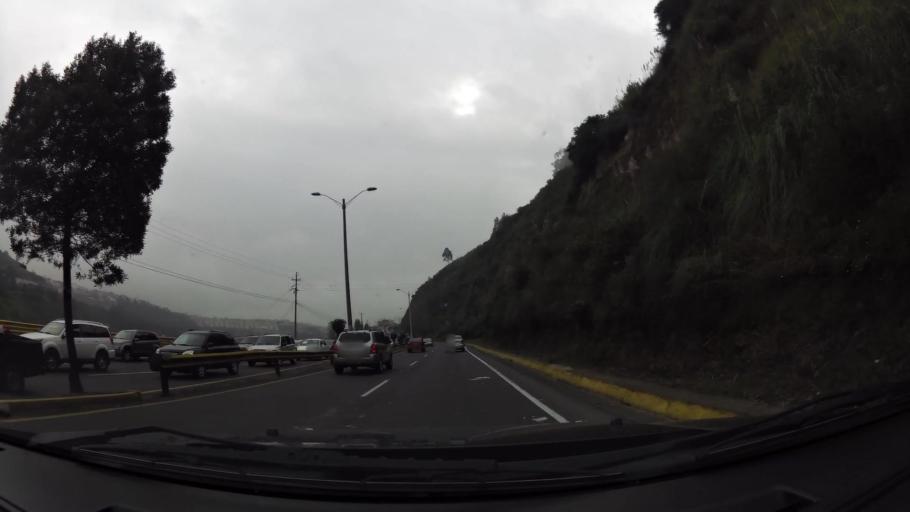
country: EC
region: Pichincha
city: Quito
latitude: -0.2298
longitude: -78.4972
